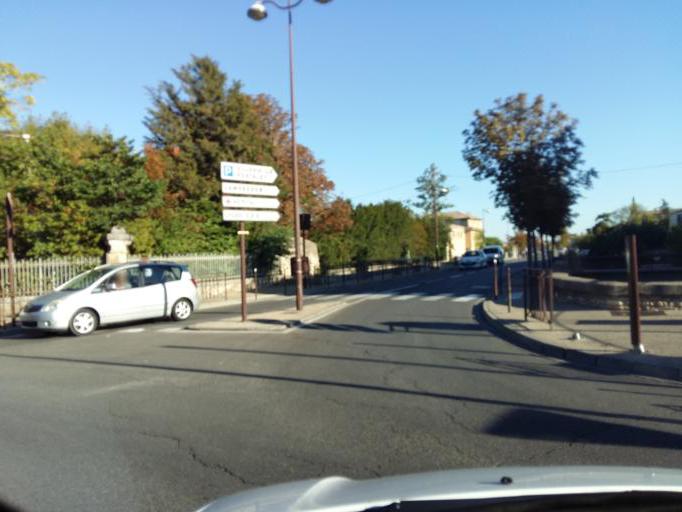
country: FR
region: Provence-Alpes-Cote d'Azur
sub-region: Departement du Vaucluse
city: L'Isle-sur-la-Sorgue
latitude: 43.9183
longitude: 5.0477
